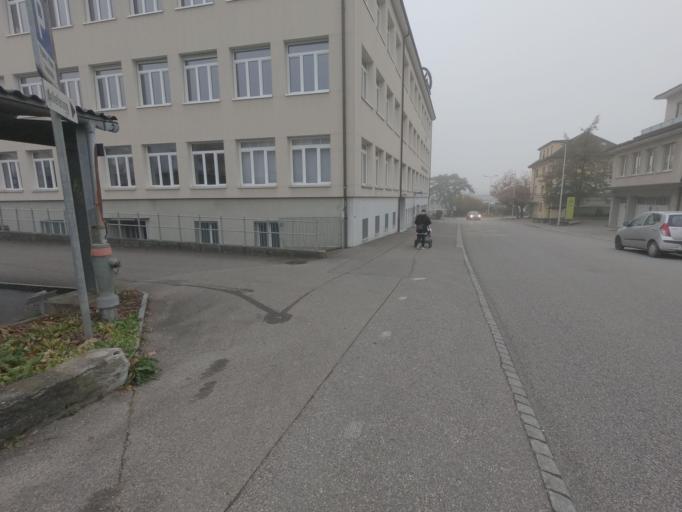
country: CH
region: Solothurn
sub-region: Bezirk Lebern
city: Grenchen
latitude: 47.1970
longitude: 7.4011
